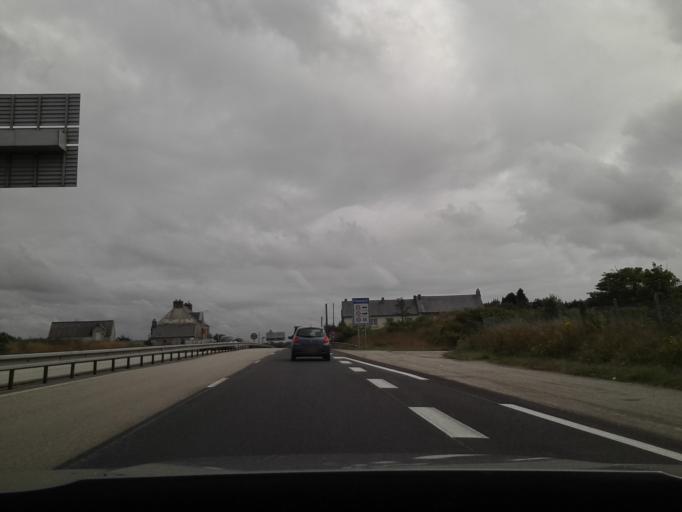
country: FR
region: Lower Normandy
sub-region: Departement de la Manche
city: La Glacerie
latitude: 49.5972
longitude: -1.5967
